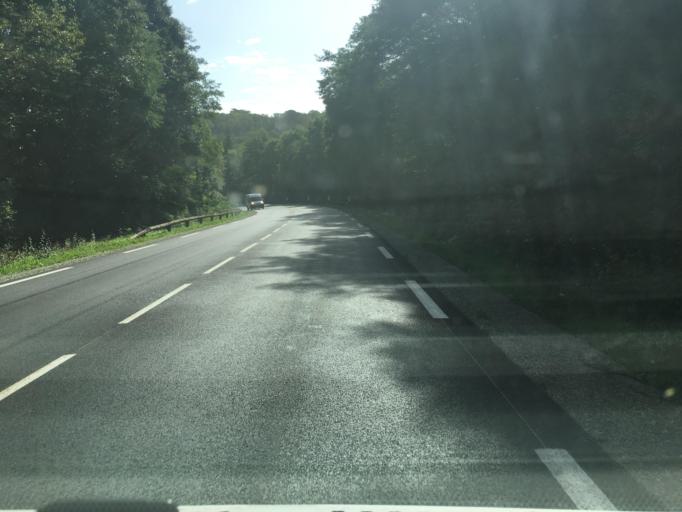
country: FR
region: Brittany
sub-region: Departement du Finistere
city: La Foret-Fouesnant
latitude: 47.9151
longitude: -3.9502
